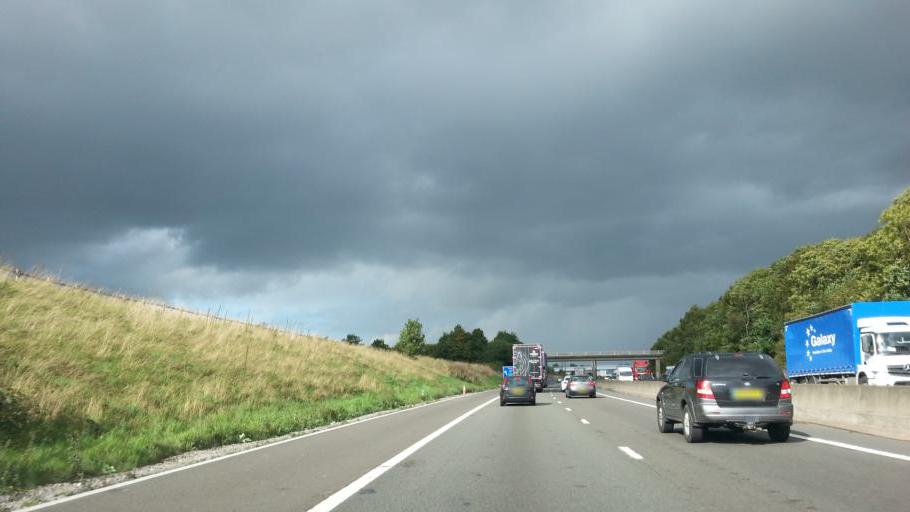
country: GB
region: England
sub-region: Warwickshire
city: Kingsbury
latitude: 52.5933
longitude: -1.6532
